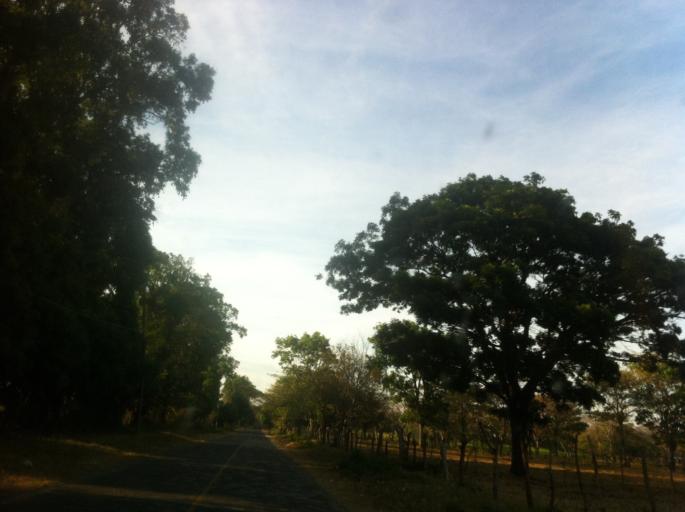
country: NI
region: Rivas
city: Buenos Aires
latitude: 11.4628
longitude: -85.8440
